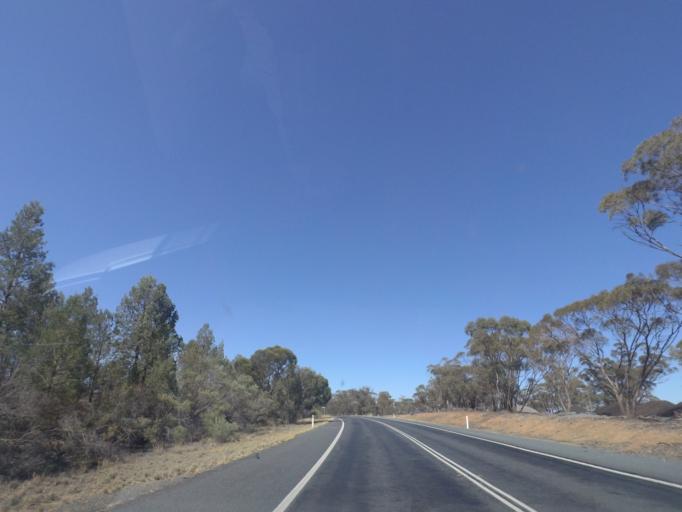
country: AU
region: New South Wales
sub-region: Bland
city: West Wyalong
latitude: -34.1176
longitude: 147.1303
